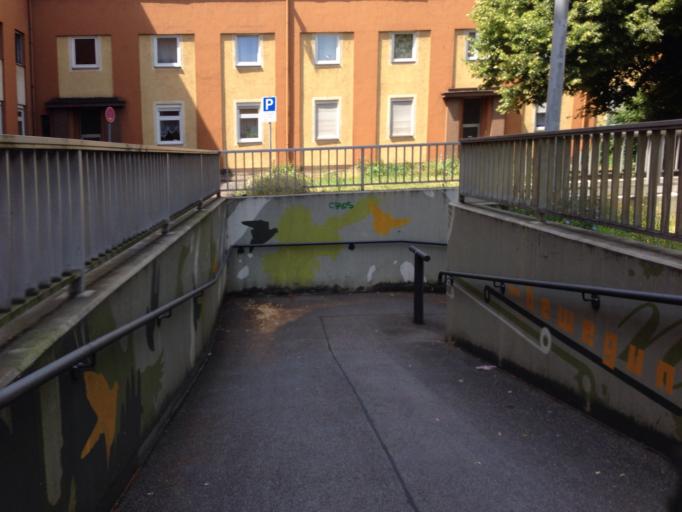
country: DE
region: Hesse
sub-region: Regierungsbezirk Darmstadt
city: Hanau am Main
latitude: 50.1243
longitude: 8.9170
